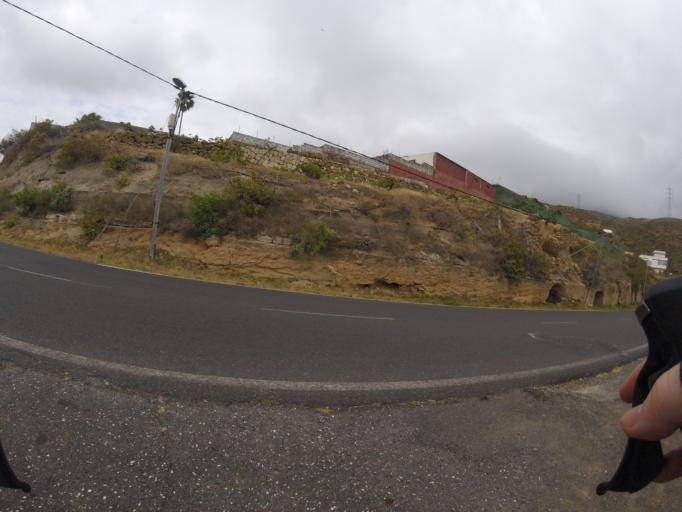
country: ES
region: Canary Islands
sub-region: Provincia de Santa Cruz de Tenerife
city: Guimar
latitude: 28.2876
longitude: -16.4048
